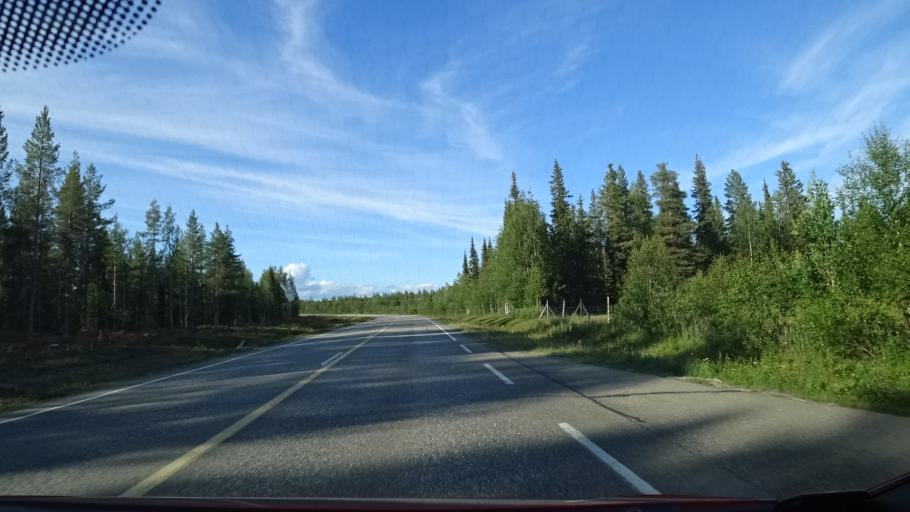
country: FI
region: Lapland
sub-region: Pohjois-Lappi
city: Sodankylae
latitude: 67.9306
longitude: 26.7634
